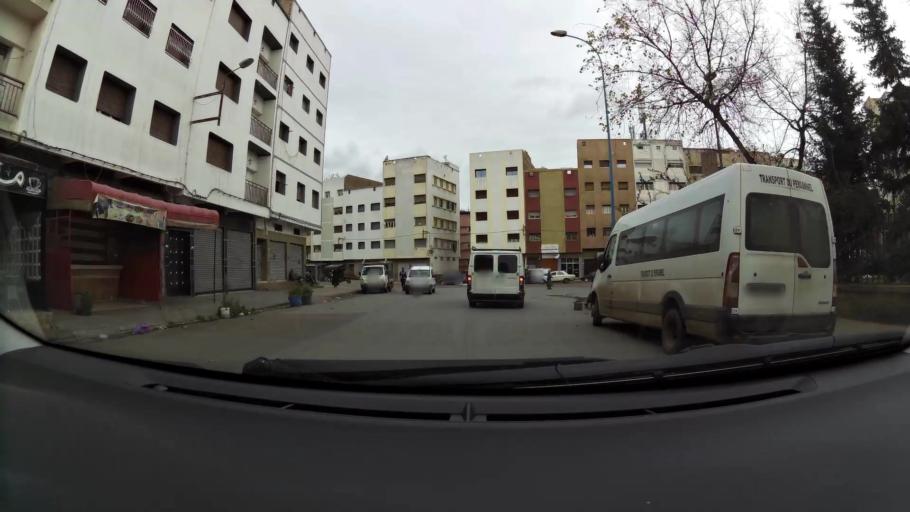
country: MA
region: Grand Casablanca
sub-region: Casablanca
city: Casablanca
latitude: 33.5727
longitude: -7.5598
